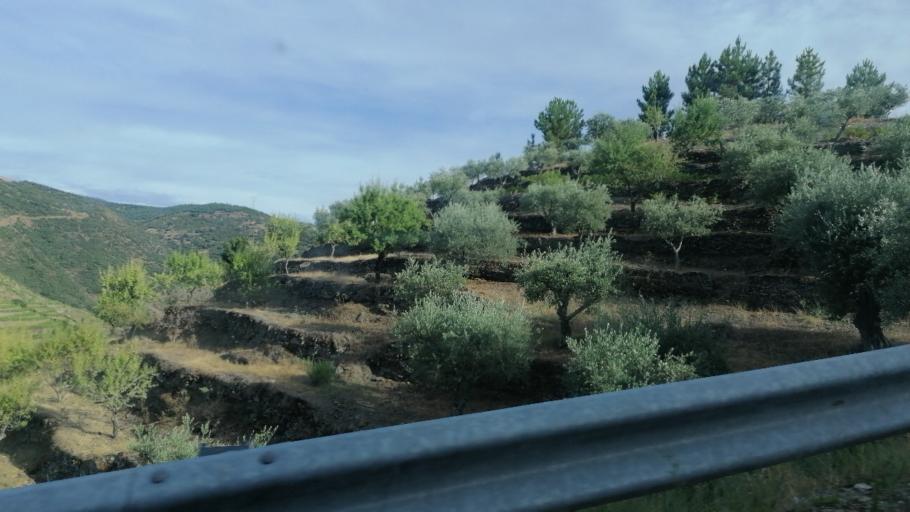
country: PT
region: Viseu
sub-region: Sao Joao da Pesqueira
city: Sao Joao da Pesqueira
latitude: 41.1141
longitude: -7.4569
